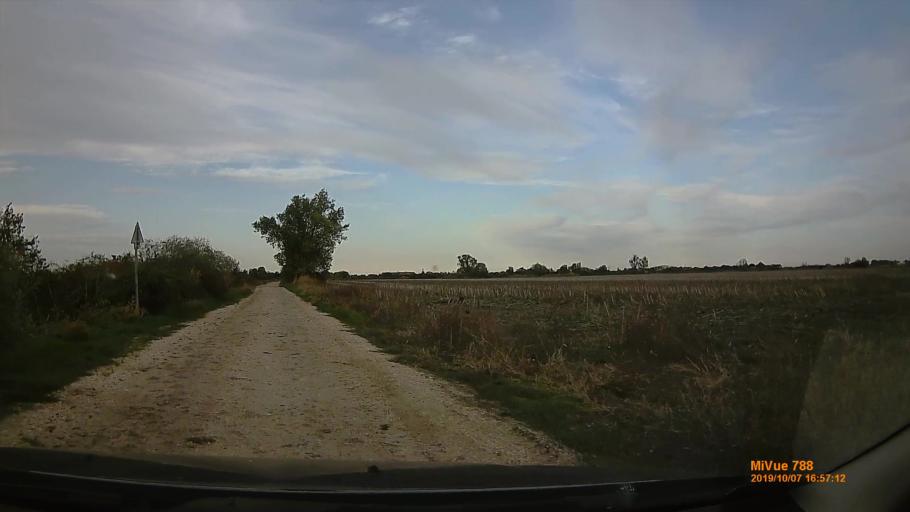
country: HU
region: Bekes
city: Szarvas
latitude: 46.8243
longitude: 20.5810
